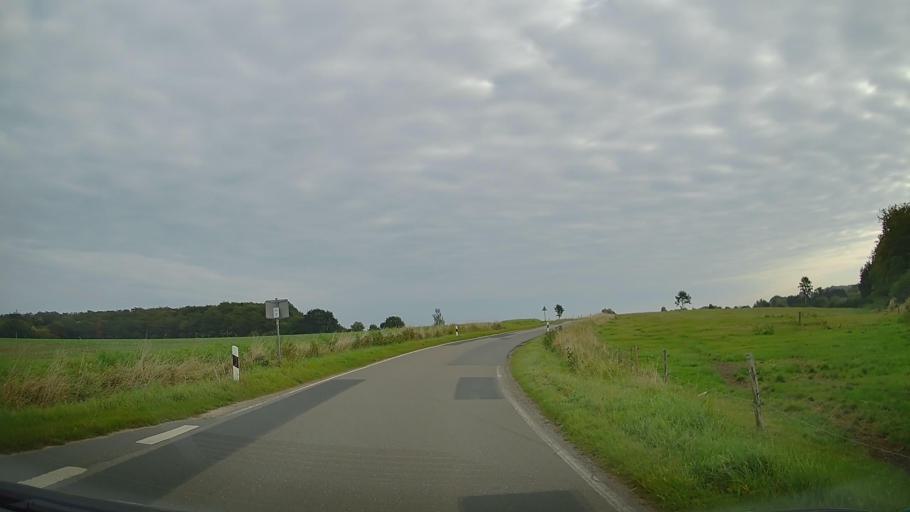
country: DE
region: Schleswig-Holstein
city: Panker
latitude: 54.3517
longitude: 10.5698
